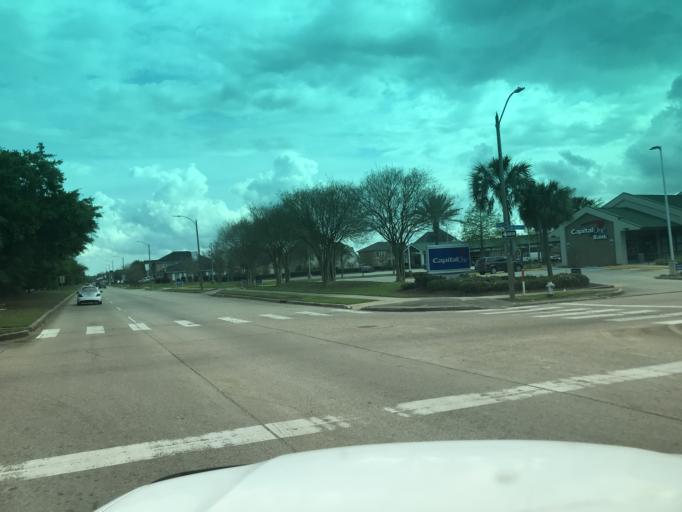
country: US
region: Louisiana
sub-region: Saint Bernard Parish
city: Chalmette
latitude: 30.0388
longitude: -89.9551
